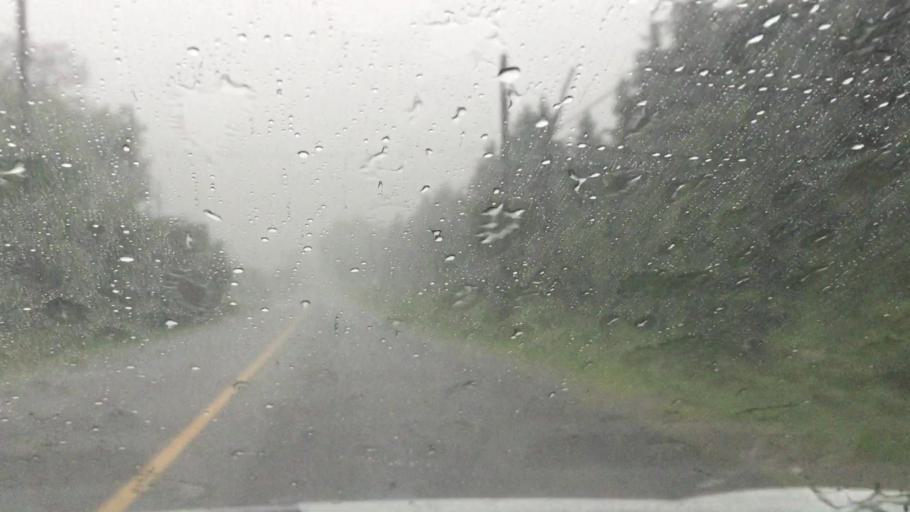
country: CA
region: Ontario
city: Markham
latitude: 43.8536
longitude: -79.2030
